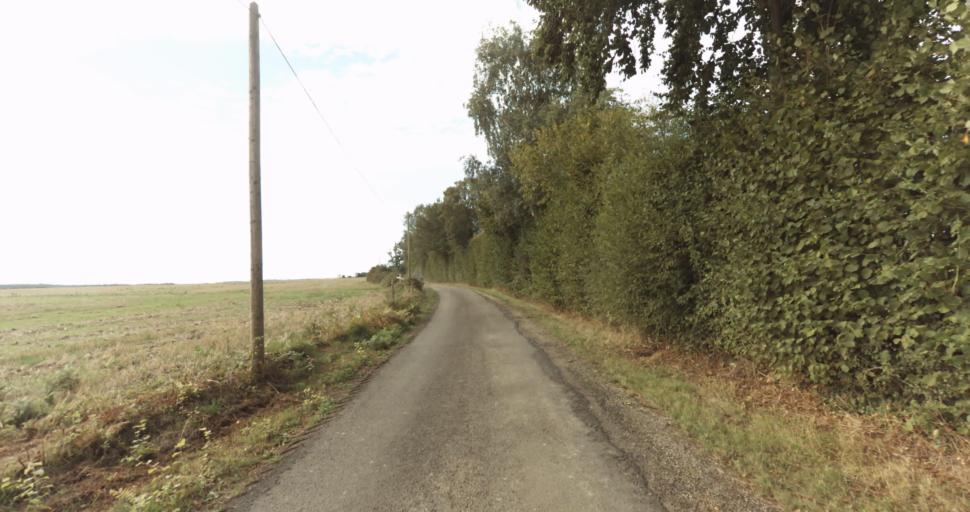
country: FR
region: Lower Normandy
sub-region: Departement de l'Orne
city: Vimoutiers
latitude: 48.8359
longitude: 0.2098
